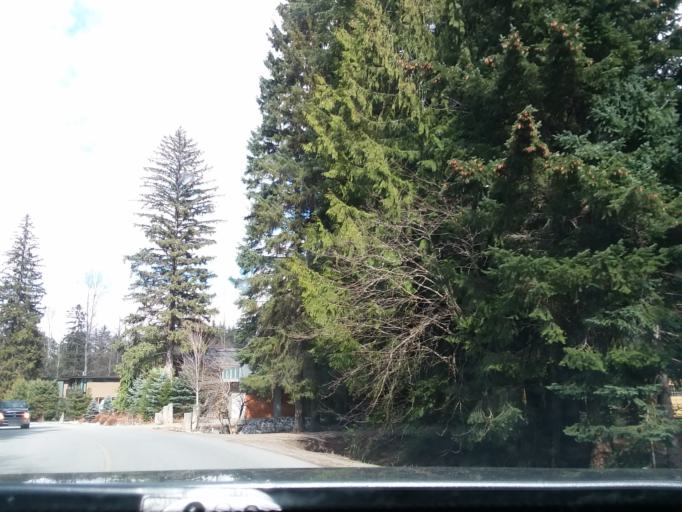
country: CA
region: British Columbia
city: Whistler
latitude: 50.1236
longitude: -122.9709
